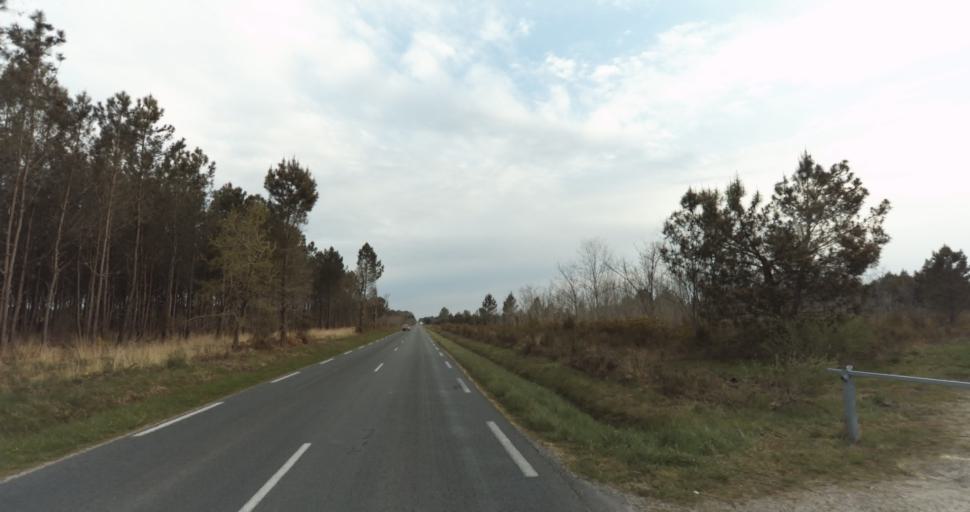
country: FR
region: Aquitaine
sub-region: Departement de la Gironde
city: Martignas-sur-Jalle
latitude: 44.7896
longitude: -0.7756
